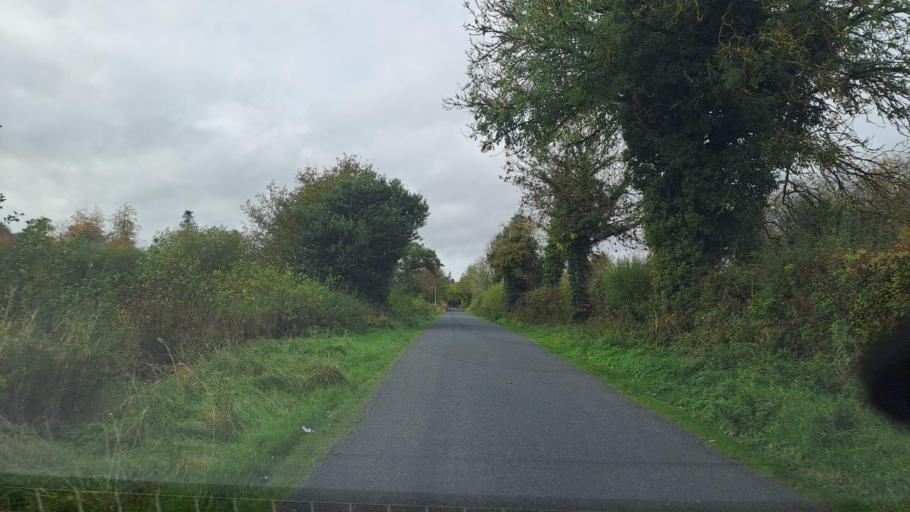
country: IE
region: Ulster
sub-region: An Cabhan
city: Bailieborough
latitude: 54.0488
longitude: -6.9131
